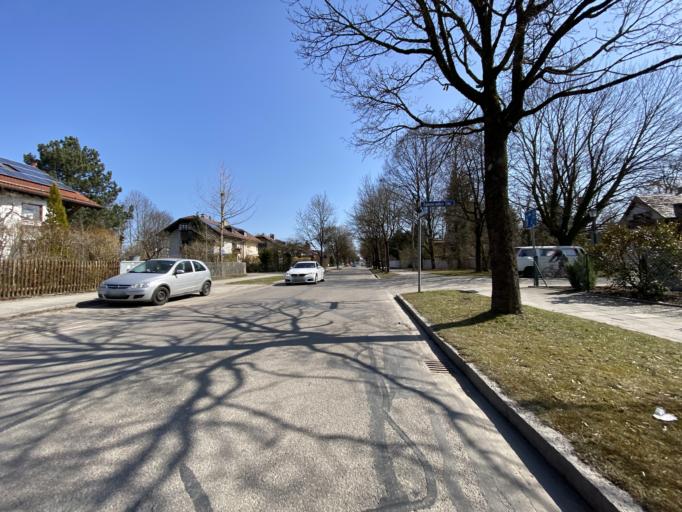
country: DE
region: Bavaria
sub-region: Upper Bavaria
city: Unterfoehring
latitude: 48.1667
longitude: 11.6599
